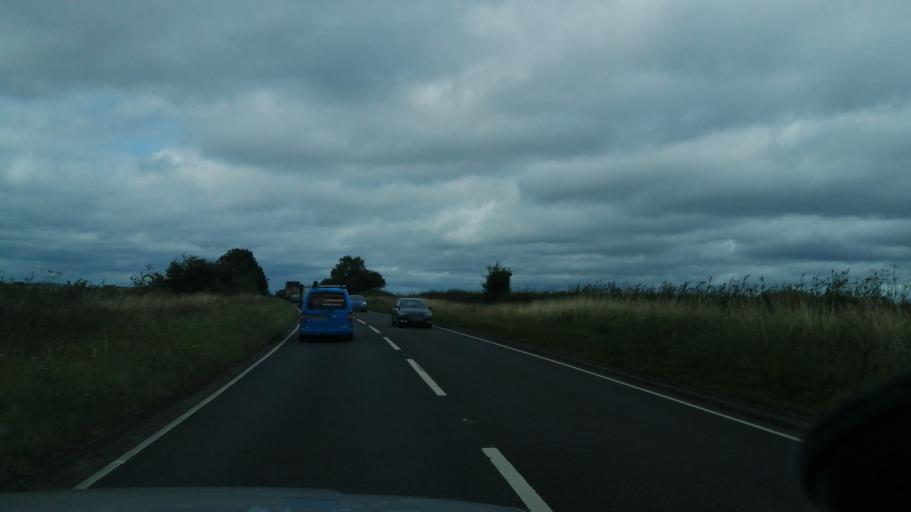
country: GB
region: England
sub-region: Herefordshire
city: Thruxton
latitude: 51.9922
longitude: -2.7901
